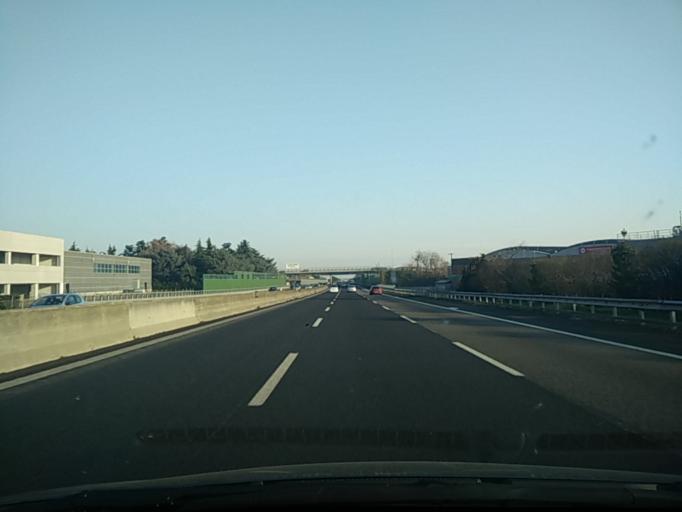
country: IT
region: Lombardy
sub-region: Provincia di Bergamo
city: Grassobbio
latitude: 45.6617
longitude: 9.7147
